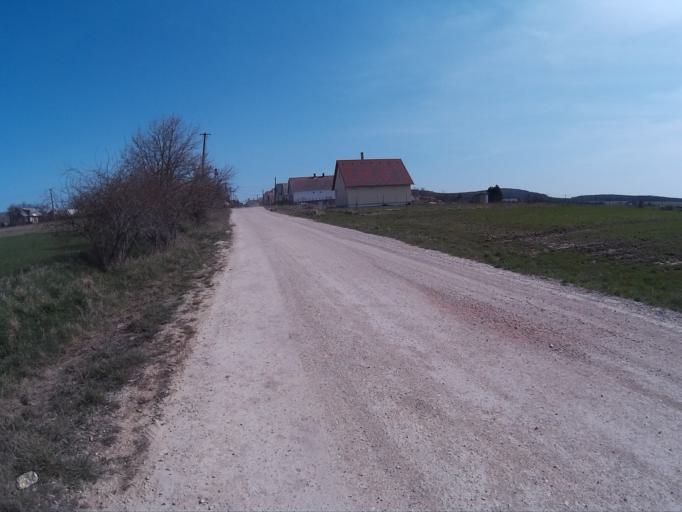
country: HU
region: Veszprem
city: Herend
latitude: 47.1896
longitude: 17.8044
